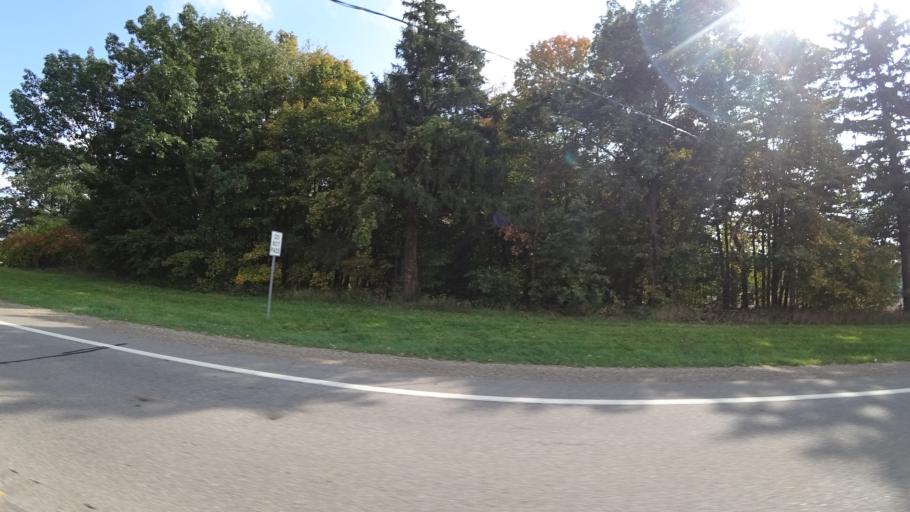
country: US
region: Michigan
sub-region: Saint Joseph County
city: Colon
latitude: 42.0091
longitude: -85.4253
